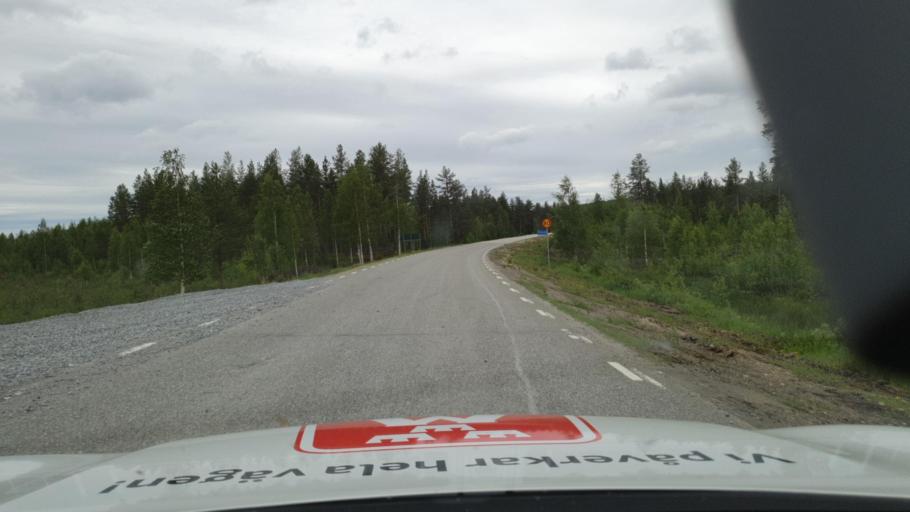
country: SE
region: Vaesterbotten
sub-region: Lycksele Kommun
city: Lycksele
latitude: 64.1628
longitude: 18.3597
